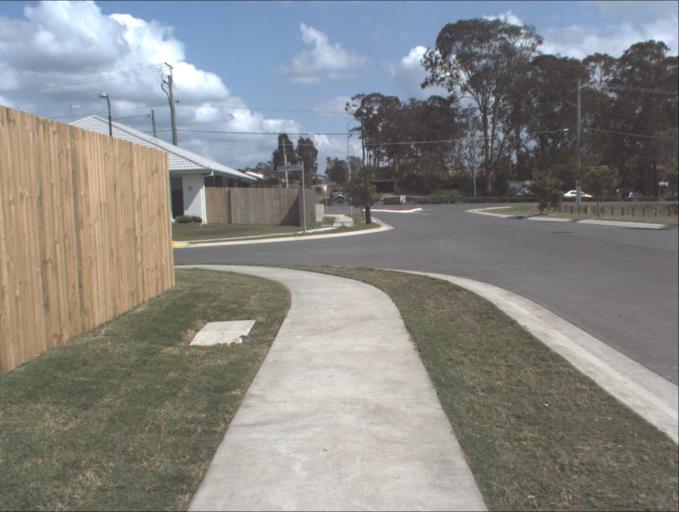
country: AU
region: Queensland
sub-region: Logan
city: Waterford West
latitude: -27.6843
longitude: 153.1383
